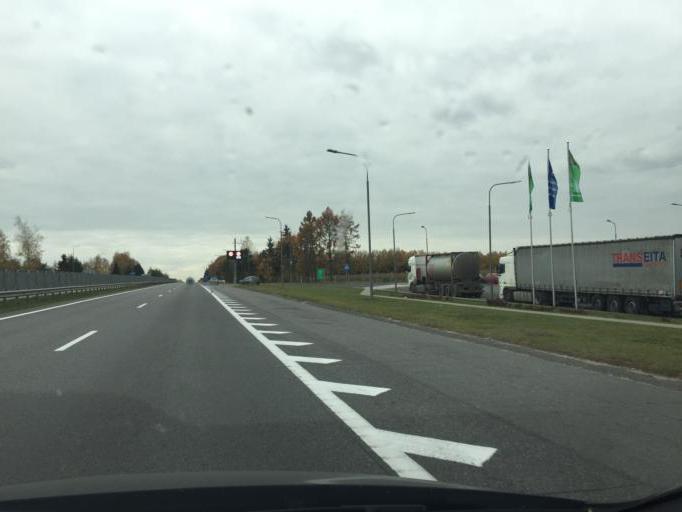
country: BY
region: Minsk
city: Samakhvalavichy
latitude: 53.7235
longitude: 27.5050
